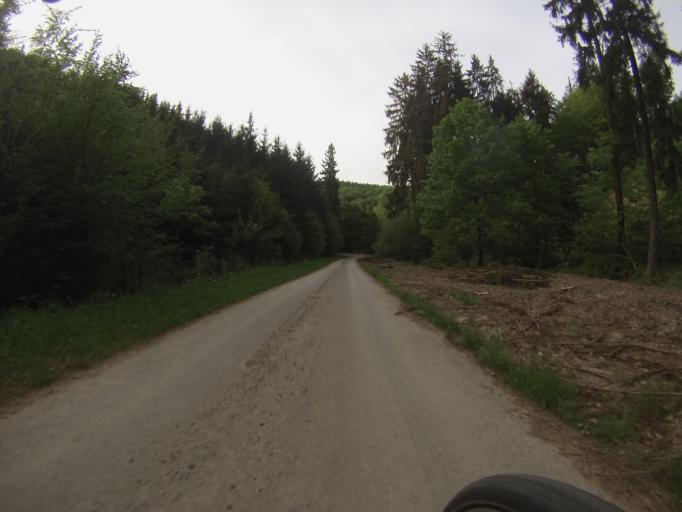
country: CZ
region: Olomoucky
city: Protivanov
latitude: 49.4742
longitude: 16.8880
